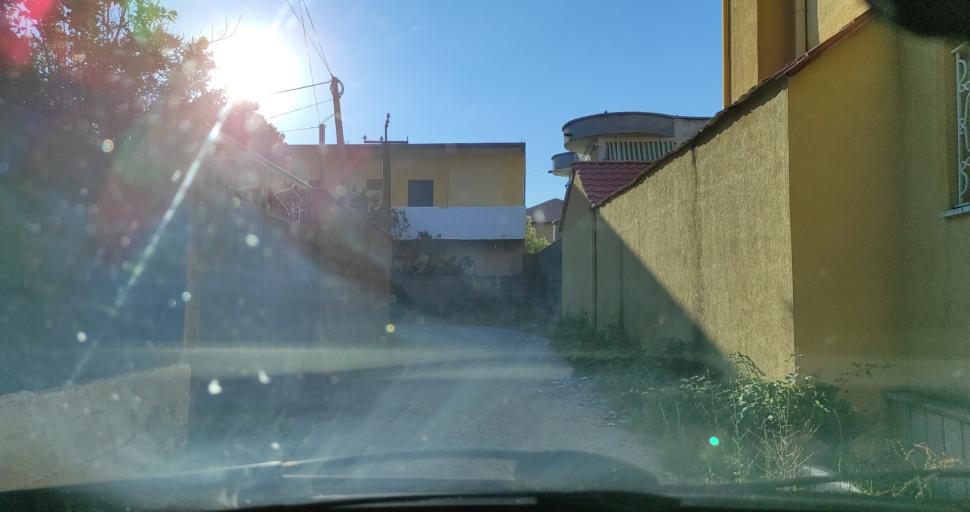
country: AL
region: Shkoder
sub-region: Rrethi i Shkodres
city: Velipoje
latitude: 41.8639
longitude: 19.4374
